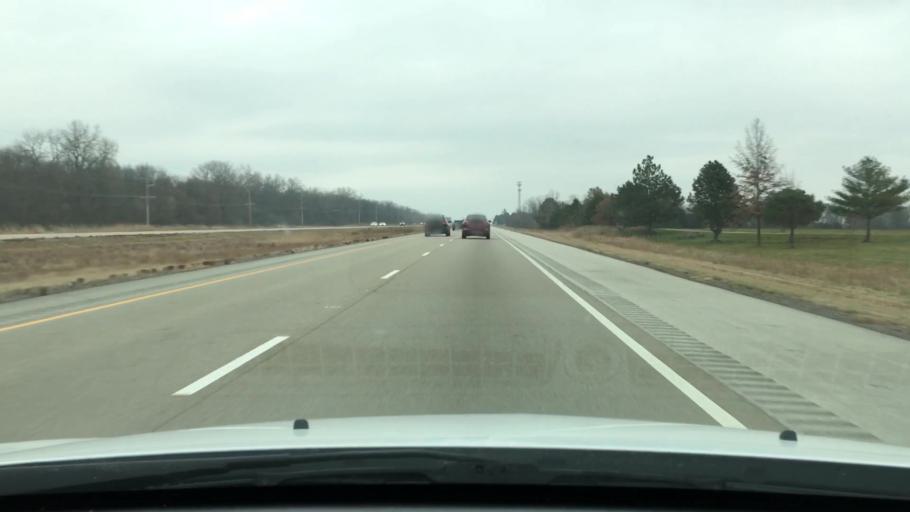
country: US
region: Illinois
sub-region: Logan County
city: Atlanta
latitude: 40.2375
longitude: -89.2580
